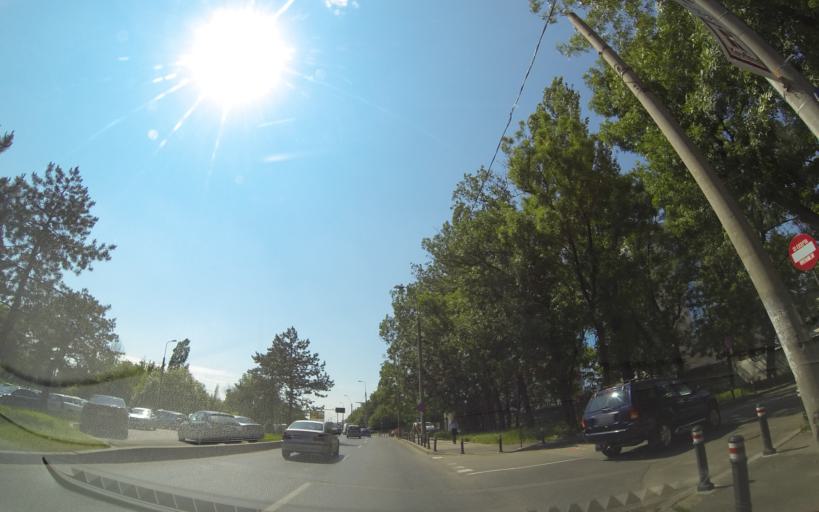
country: RO
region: Bucuresti
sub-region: Municipiul Bucuresti
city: Bucuresti
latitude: 44.4317
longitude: 26.0593
